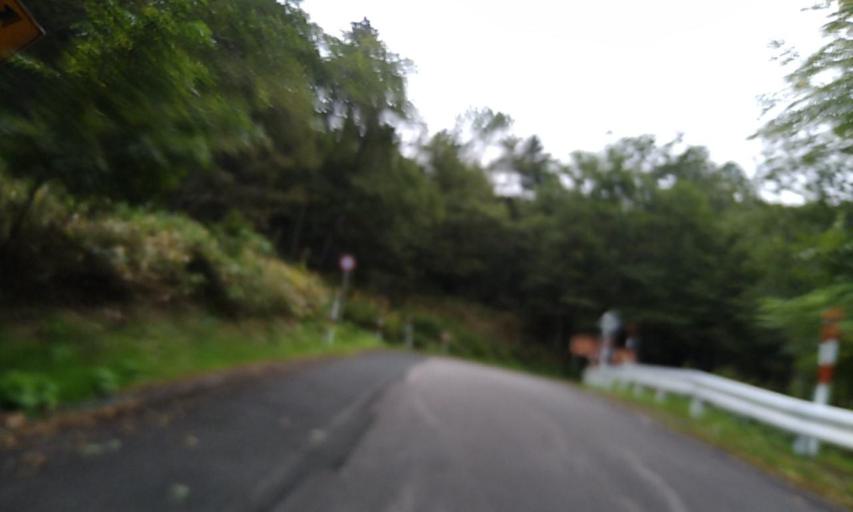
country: JP
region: Hokkaido
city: Bihoro
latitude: 43.5666
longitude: 144.1949
